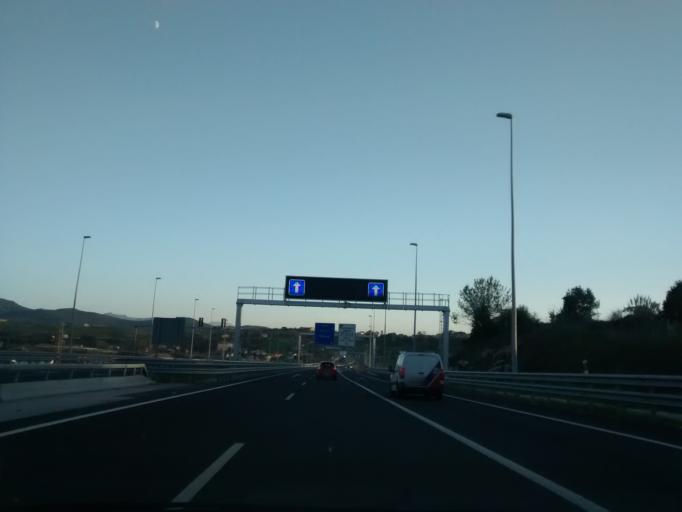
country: ES
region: Cantabria
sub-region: Provincia de Cantabria
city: Camargo
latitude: 43.4083
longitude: -3.8721
